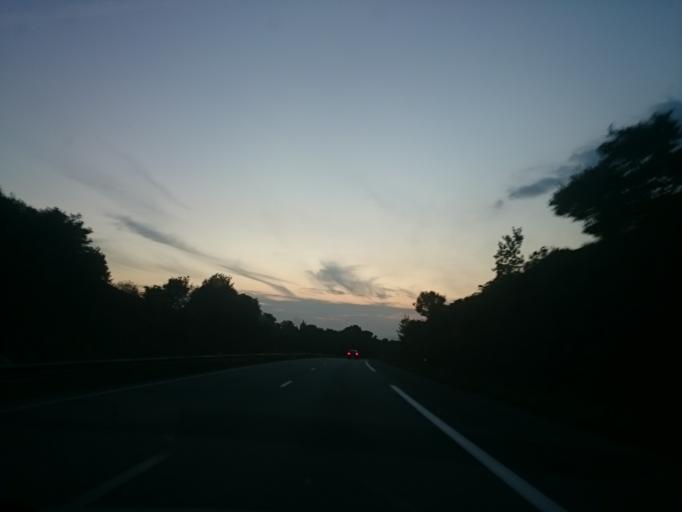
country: FR
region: Brittany
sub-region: Departement du Finistere
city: Le Faou
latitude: 48.2819
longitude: -4.1362
